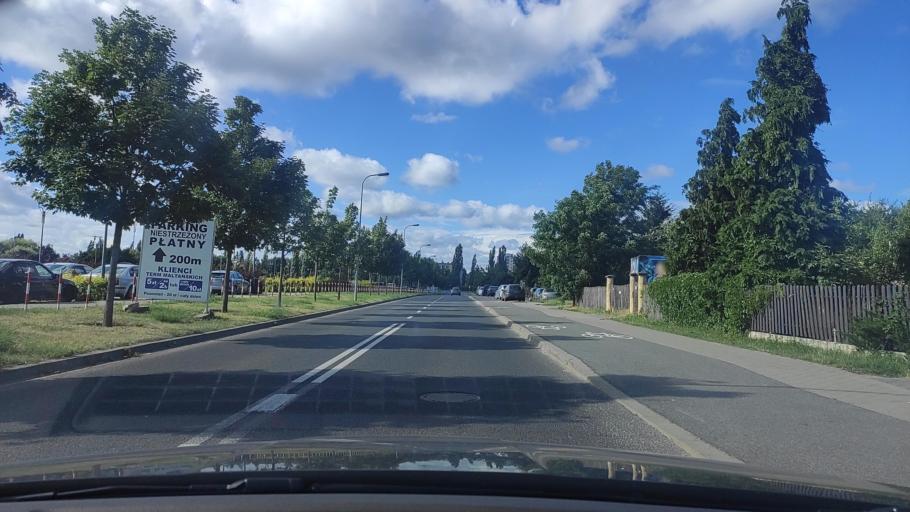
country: PL
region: Greater Poland Voivodeship
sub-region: Poznan
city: Poznan
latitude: 52.4063
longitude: 16.9767
